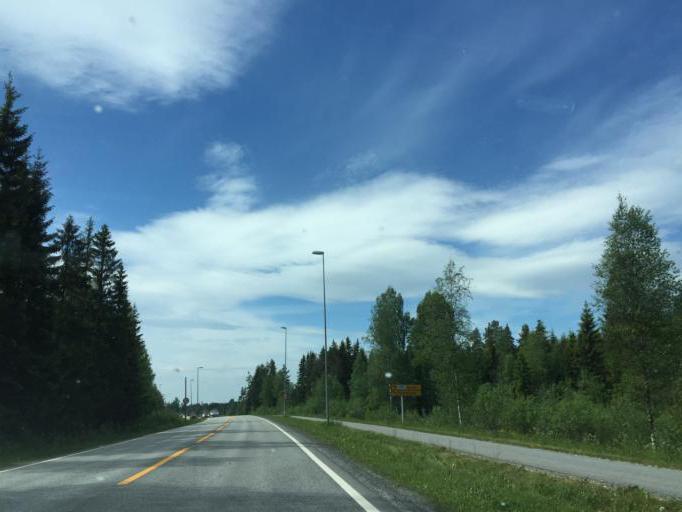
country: NO
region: Akershus
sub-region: Nes
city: Arnes
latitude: 60.1857
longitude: 11.5348
